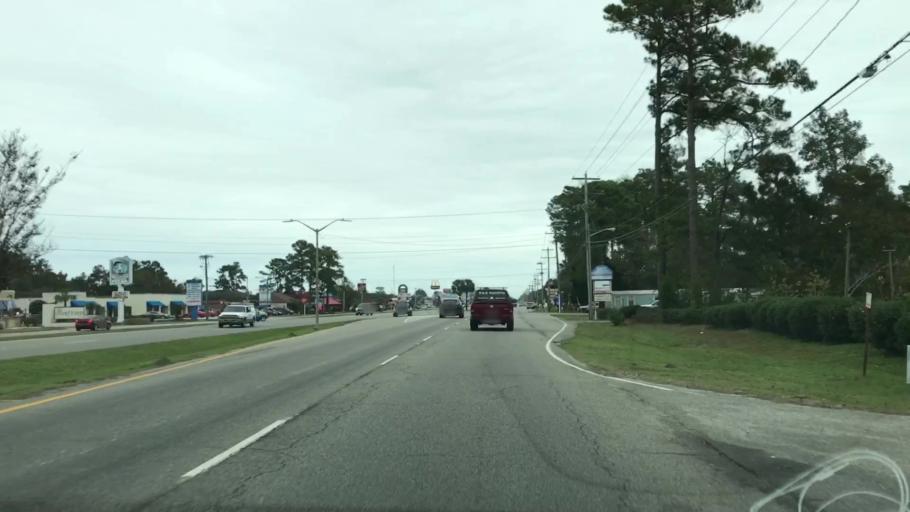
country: US
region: South Carolina
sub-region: Horry County
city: Surfside Beach
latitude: 33.6226
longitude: -78.9705
